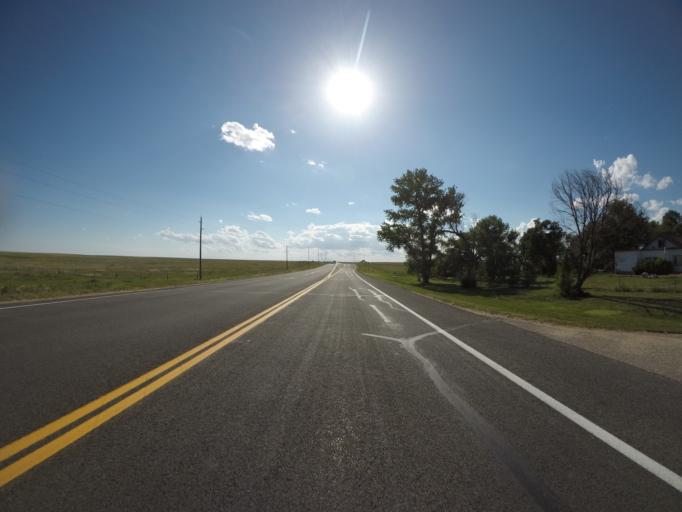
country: US
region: Colorado
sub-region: Morgan County
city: Fort Morgan
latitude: 40.6113
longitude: -103.7979
